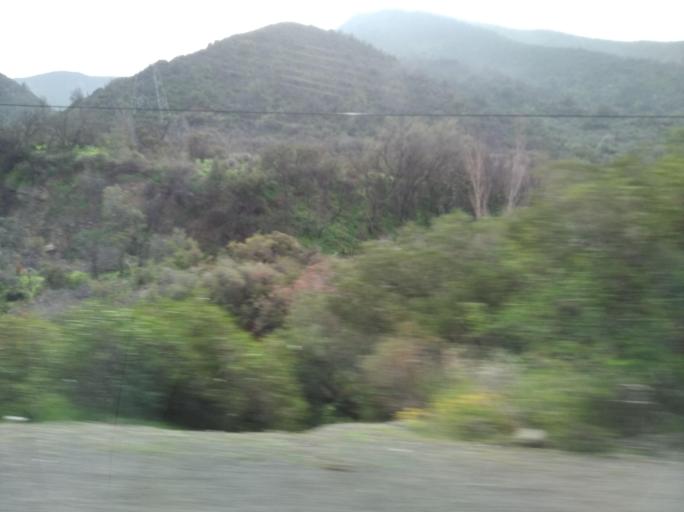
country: CL
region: Valparaiso
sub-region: Provincia de San Felipe
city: Llaillay
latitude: -33.0718
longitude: -70.9662
